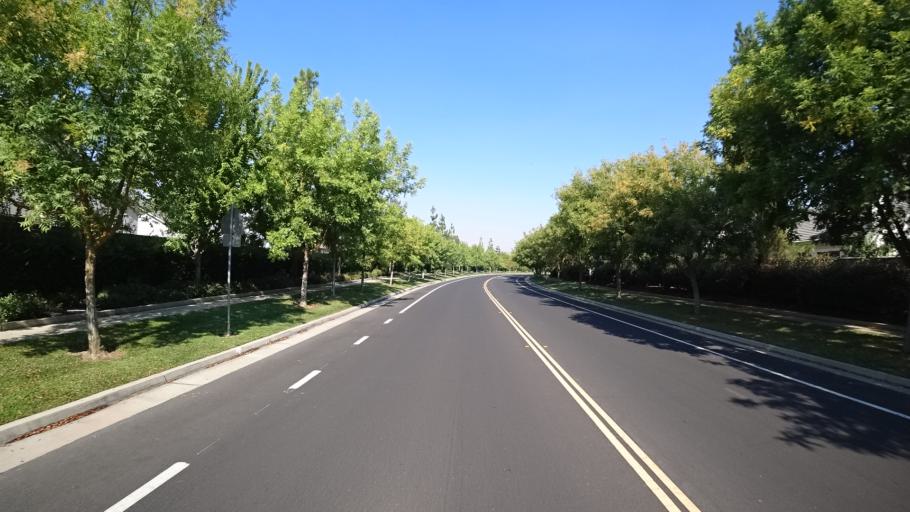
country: US
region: California
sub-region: Sacramento County
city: Laguna
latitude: 38.3842
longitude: -121.4320
